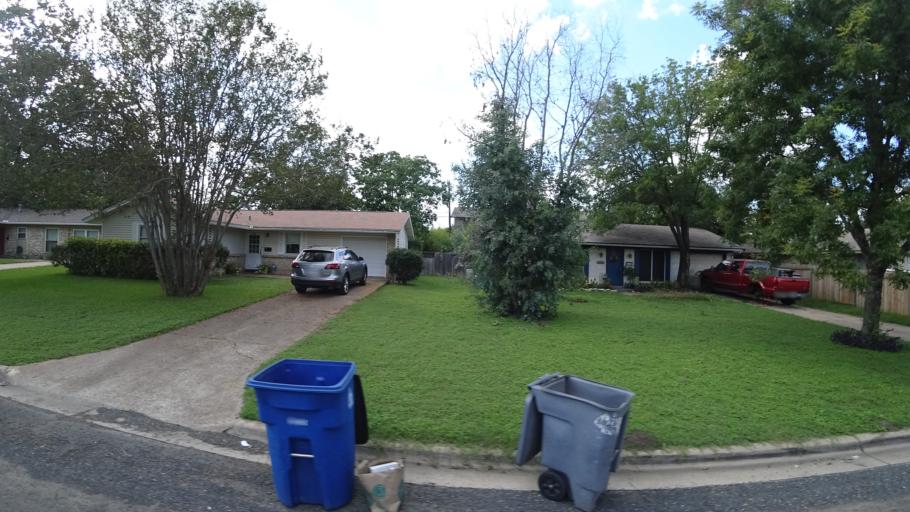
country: US
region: Texas
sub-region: Travis County
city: Wells Branch
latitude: 30.3623
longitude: -97.7111
